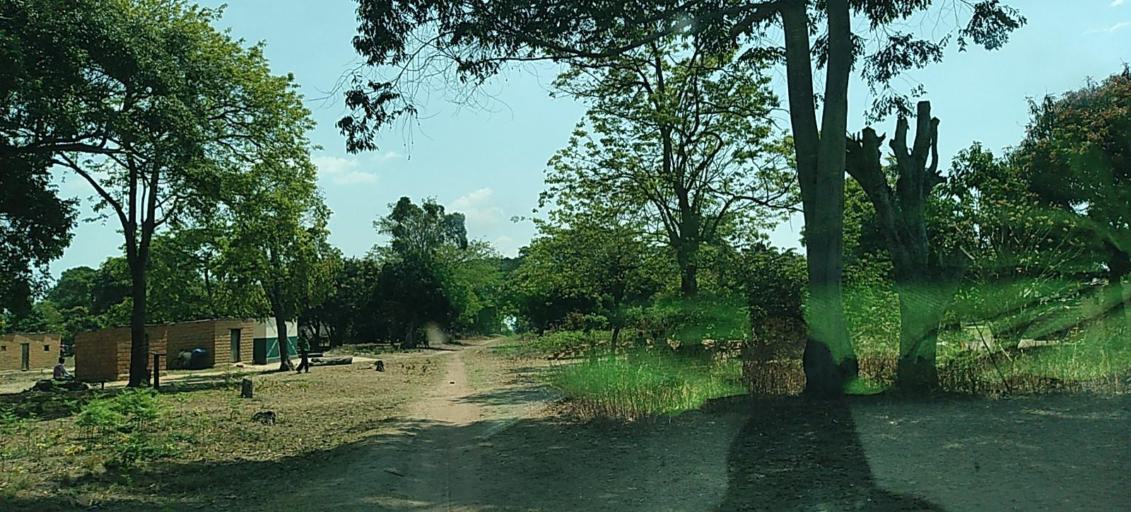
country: CD
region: Katanga
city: Kolwezi
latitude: -11.2812
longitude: 25.1510
